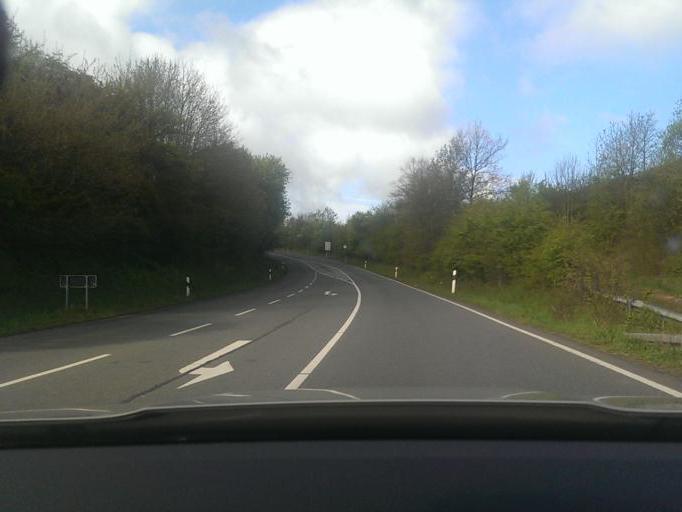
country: DE
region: Lower Saxony
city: Rehren
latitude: 52.2300
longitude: 9.2371
